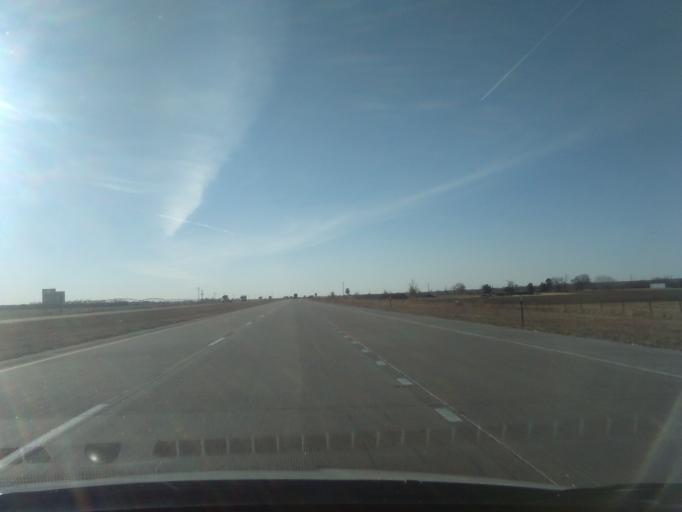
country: US
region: Colorado
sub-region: Sedgwick County
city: Julesburg
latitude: 41.0464
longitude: -102.0791
